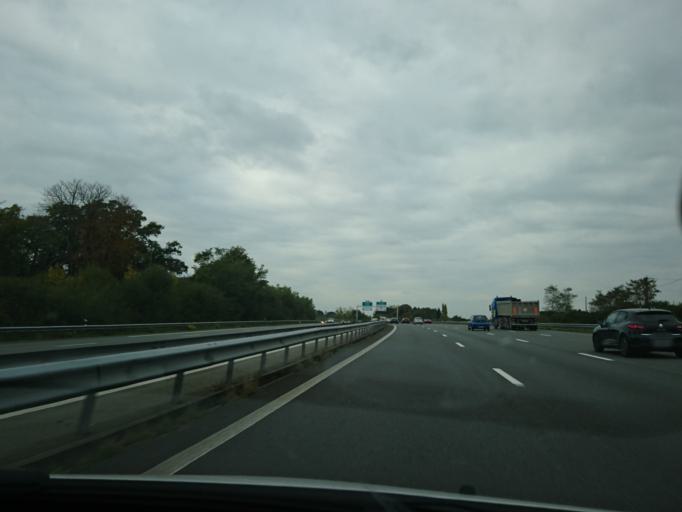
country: FR
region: Pays de la Loire
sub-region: Departement de la Loire-Atlantique
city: Savenay
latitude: 47.3668
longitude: -1.9082
